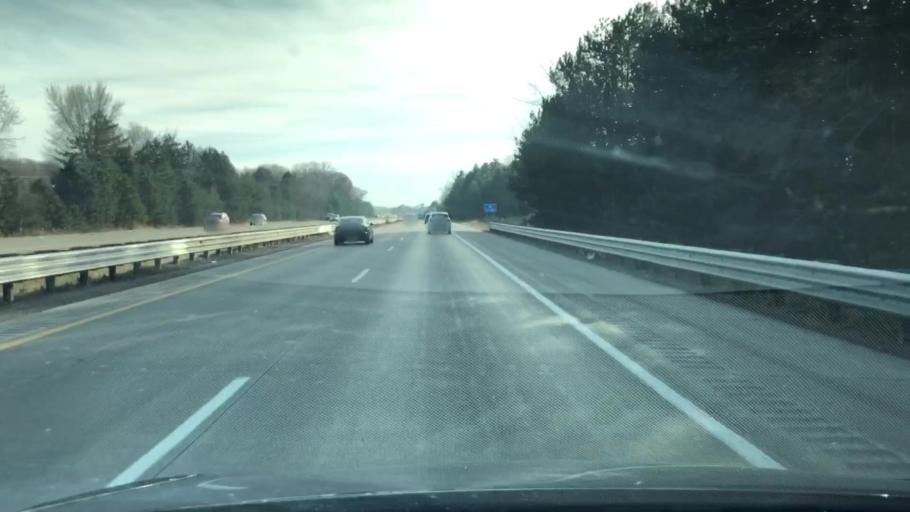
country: US
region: Michigan
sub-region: Genesee County
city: Lake Fenton
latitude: 42.9273
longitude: -83.7252
